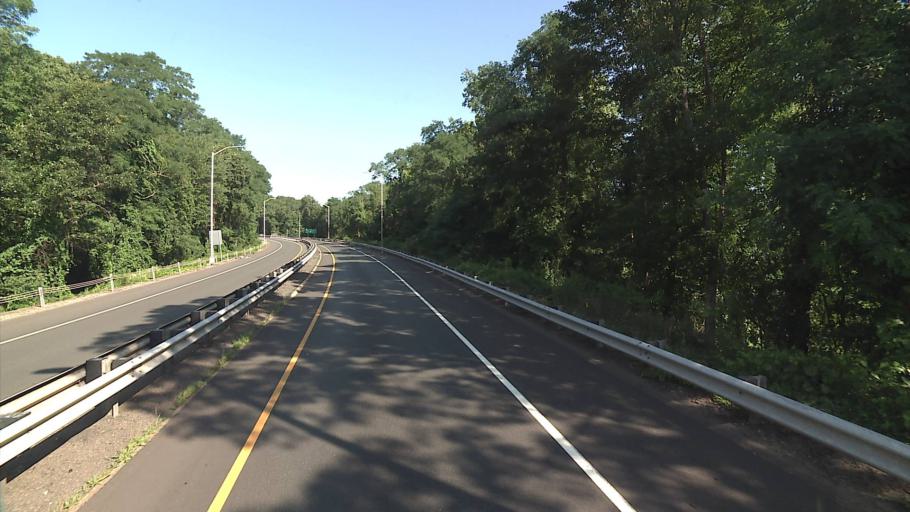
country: US
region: Connecticut
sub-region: Hartford County
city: Tariffville
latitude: 41.9229
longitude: -72.6945
